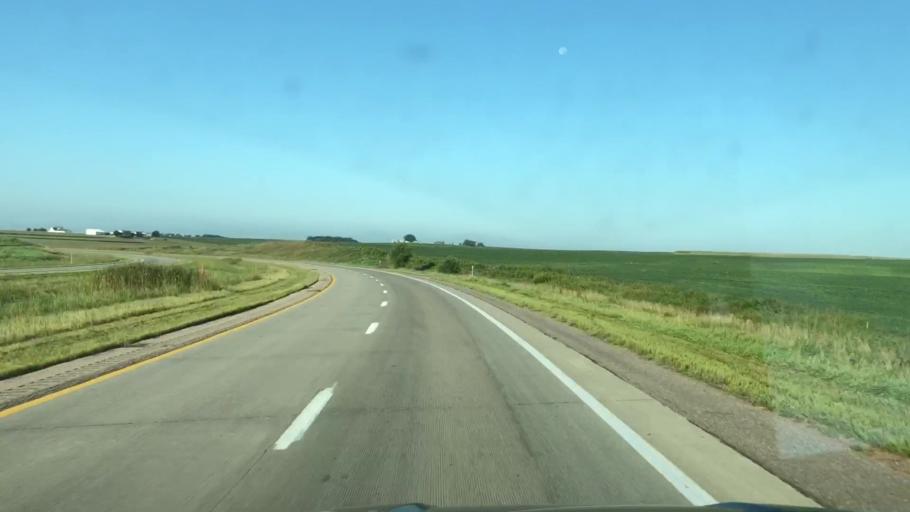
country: US
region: Iowa
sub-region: Sioux County
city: Alton
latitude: 42.9741
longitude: -96.0186
